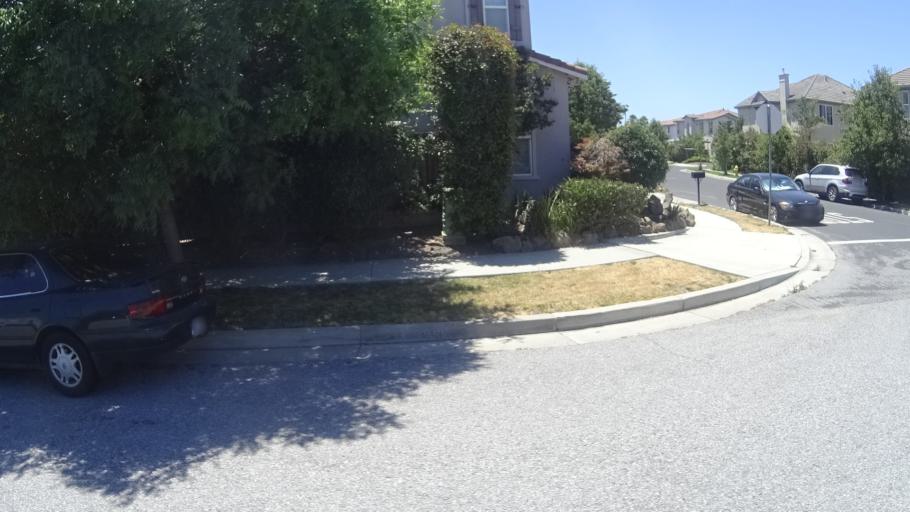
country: US
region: California
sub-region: Santa Clara County
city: Seven Trees
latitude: 37.2646
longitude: -121.8460
